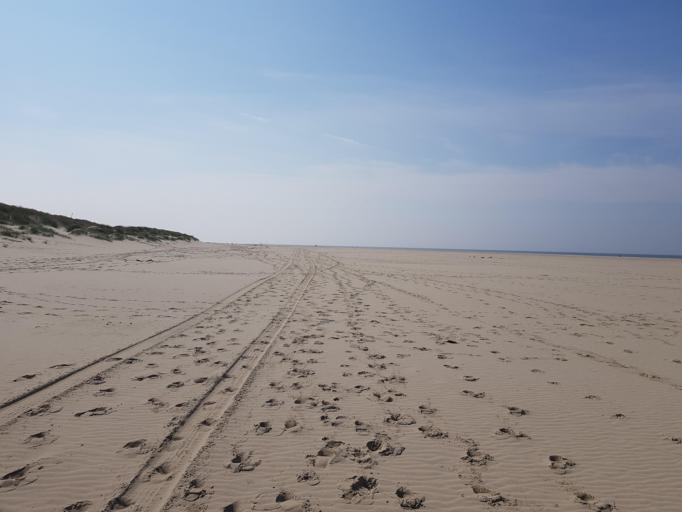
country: NL
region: North Holland
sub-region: Gemeente Texel
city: Den Burg
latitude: 53.1759
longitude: 4.8364
